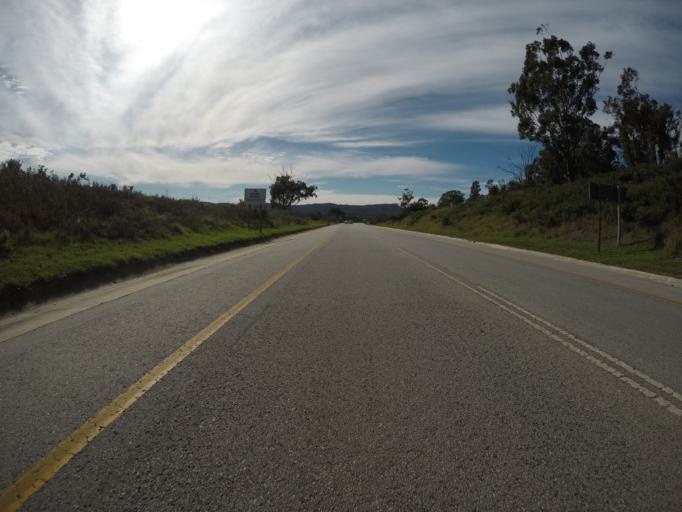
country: ZA
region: Eastern Cape
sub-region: Cacadu District Municipality
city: Jeffrey's Bay
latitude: -33.8931
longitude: 25.1323
